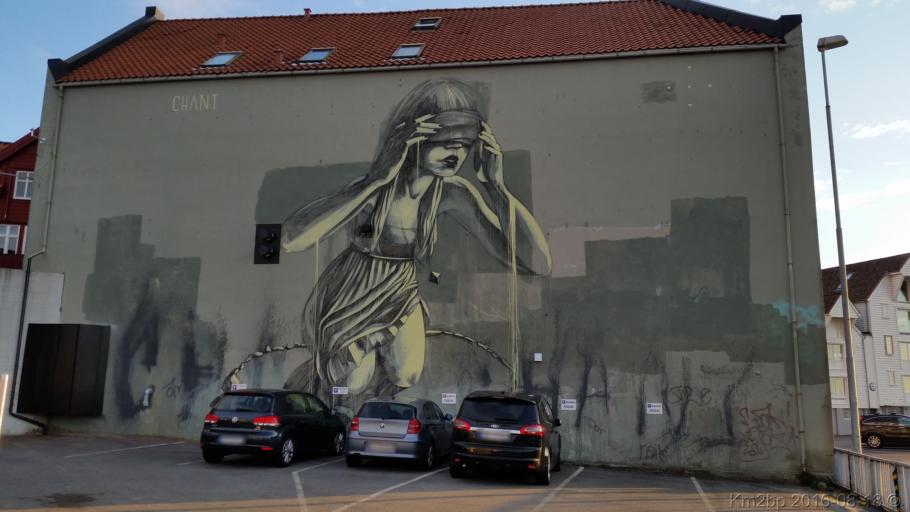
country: NO
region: Rogaland
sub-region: Stavanger
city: Stavanger
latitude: 58.9745
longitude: 5.7319
